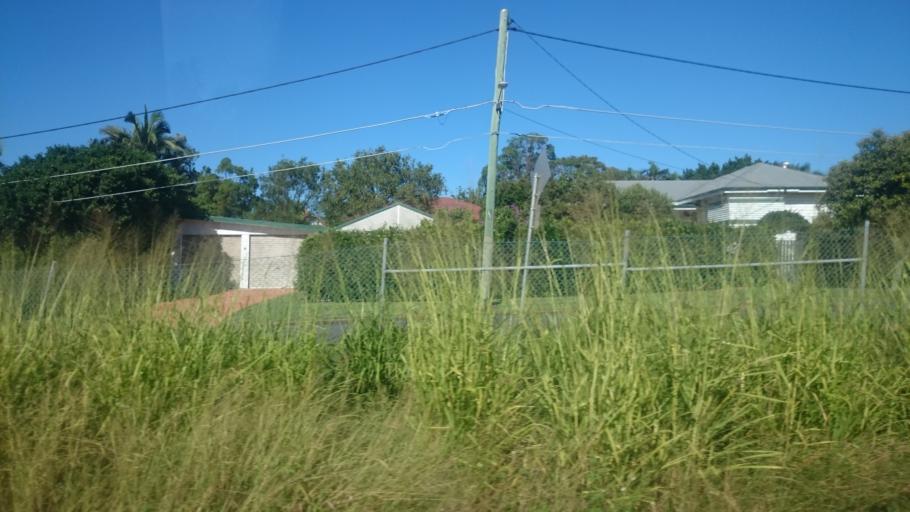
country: AU
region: Queensland
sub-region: Brisbane
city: Wynnum
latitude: -27.4377
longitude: 153.1638
